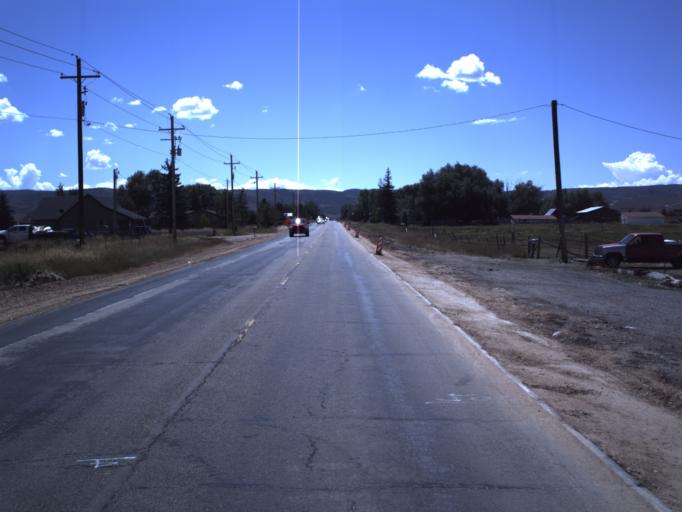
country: US
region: Utah
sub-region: Summit County
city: Francis
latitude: 40.6232
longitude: -111.2807
